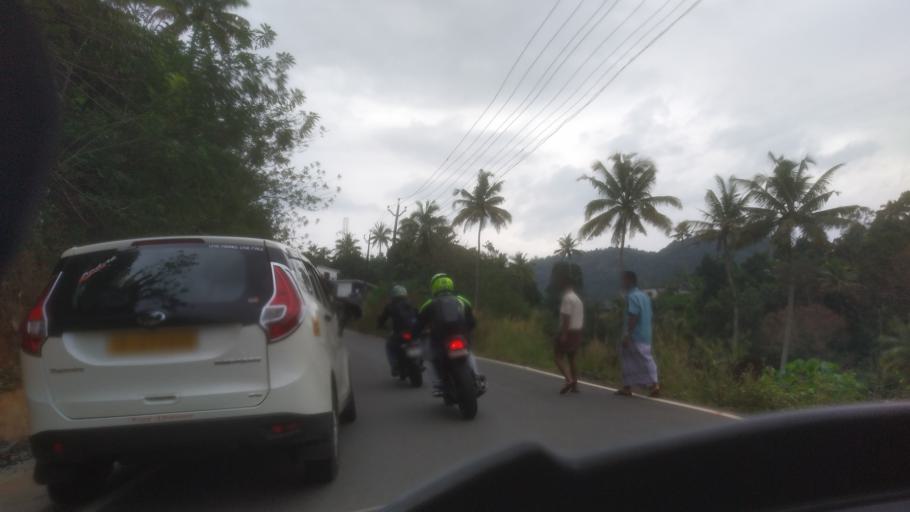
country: IN
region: Kerala
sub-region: Idukki
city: Idukki
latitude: 9.9593
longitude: 77.0093
